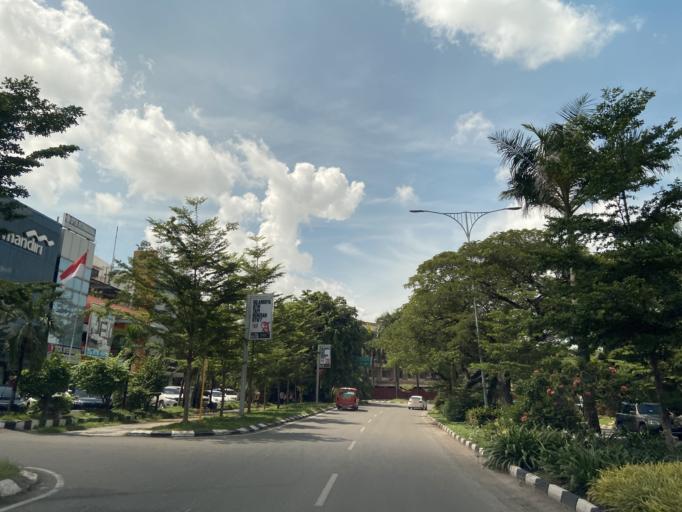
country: SG
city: Singapore
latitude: 1.1503
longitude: 104.0086
